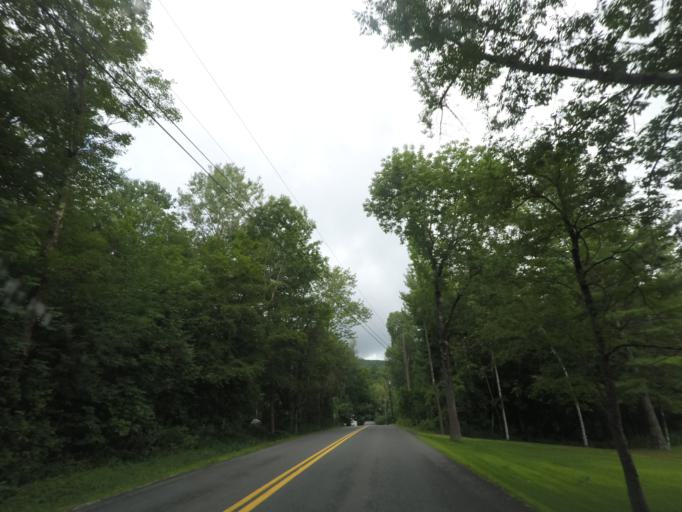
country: US
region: Massachusetts
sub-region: Berkshire County
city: Lanesborough
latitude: 42.5658
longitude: -73.2562
